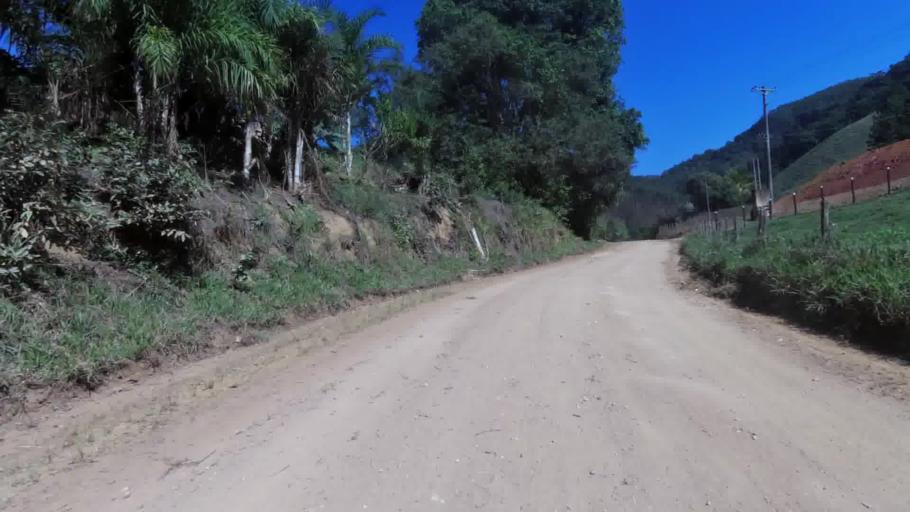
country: BR
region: Espirito Santo
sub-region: Alfredo Chaves
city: Alfredo Chaves
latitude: -20.5323
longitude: -40.8453
